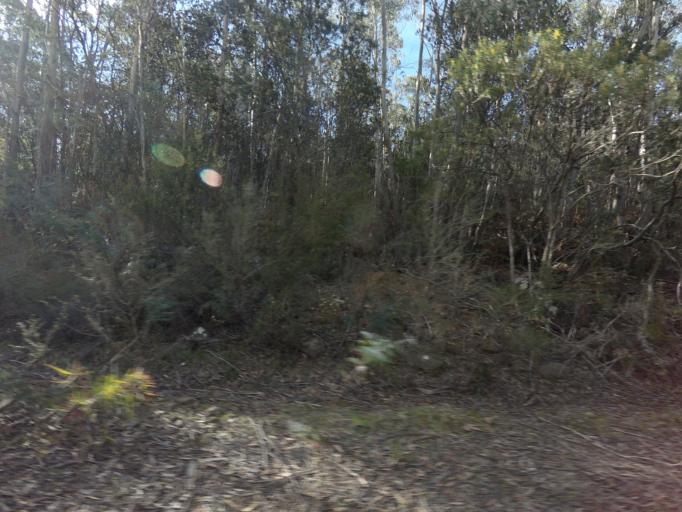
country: AU
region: Tasmania
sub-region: Break O'Day
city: St Helens
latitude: -41.8472
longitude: 148.0560
